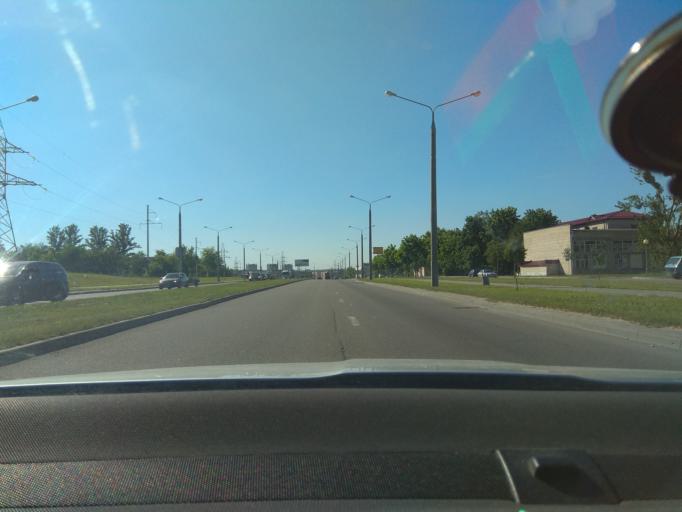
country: BY
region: Grodnenskaya
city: Hrodna
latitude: 53.6513
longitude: 23.7986
